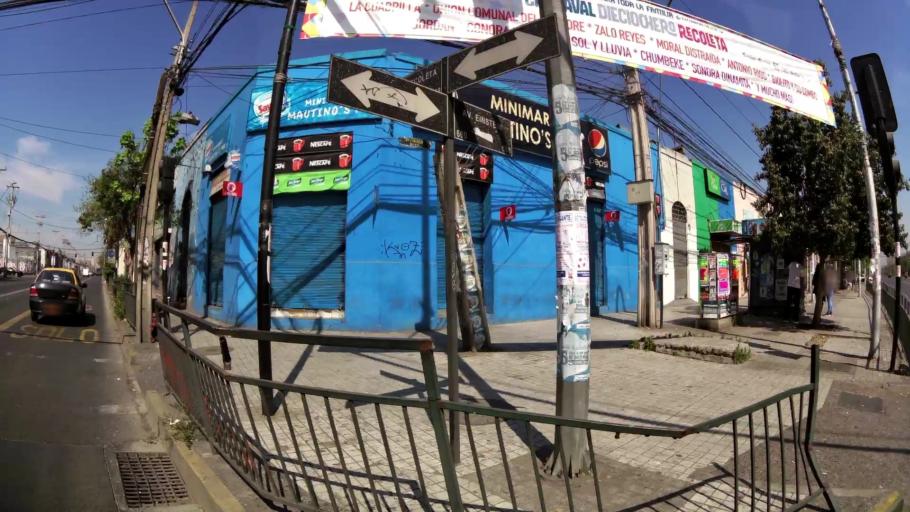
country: CL
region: Santiago Metropolitan
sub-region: Provincia de Santiago
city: Santiago
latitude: -33.4064
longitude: -70.6431
